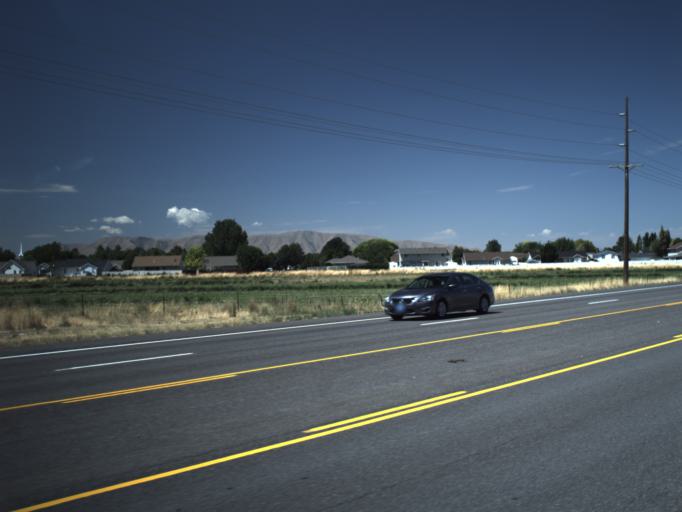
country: US
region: Utah
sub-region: Utah County
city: Spanish Fork
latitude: 40.1028
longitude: -111.6188
